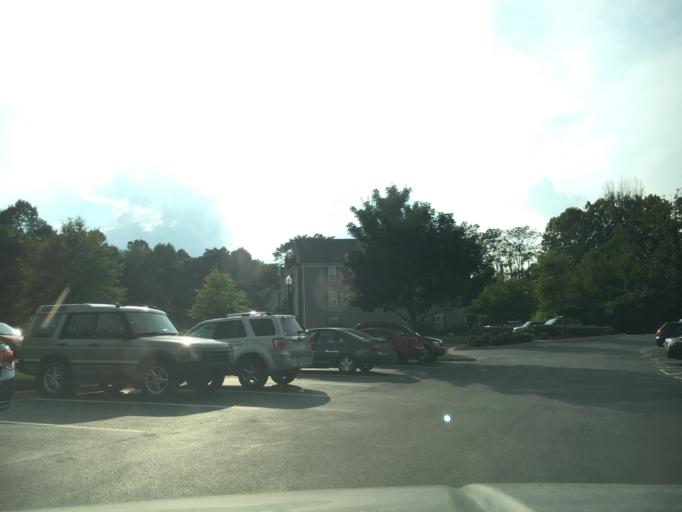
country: US
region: Virginia
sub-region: Campbell County
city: Timberlake
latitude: 37.3369
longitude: -79.2350
